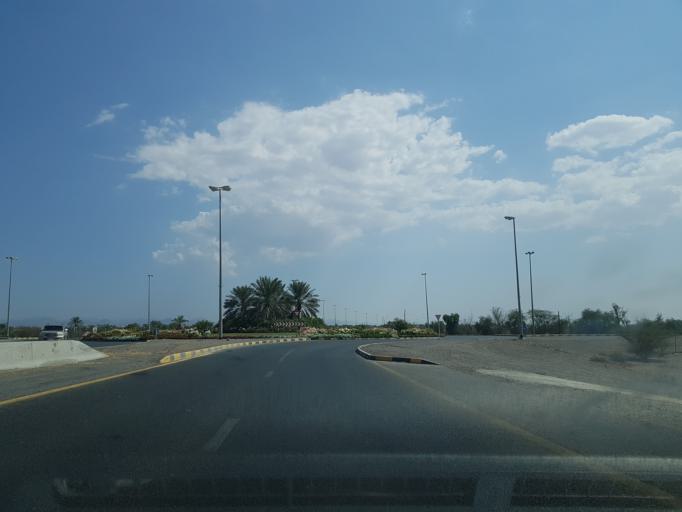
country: AE
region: Ash Shariqah
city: Adh Dhayd
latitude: 25.2436
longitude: 55.9134
